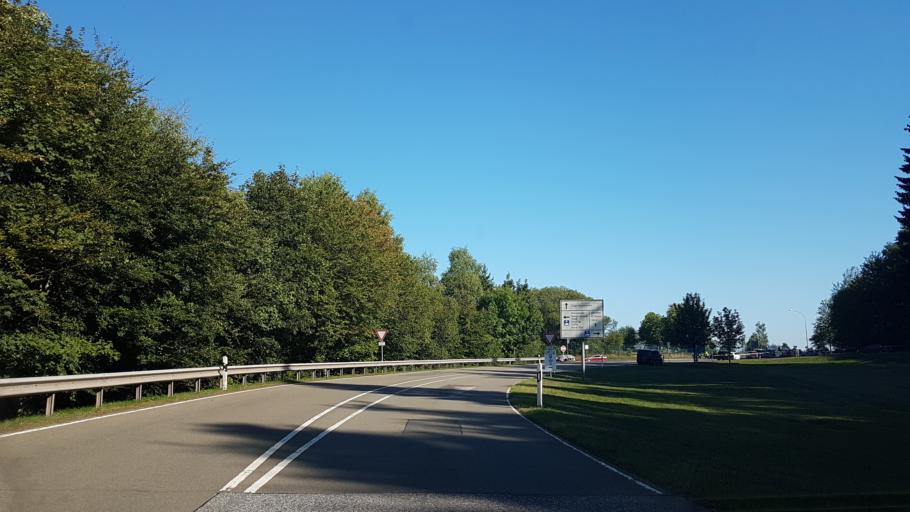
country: DE
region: Rheinland-Pfalz
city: Baumholder
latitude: 49.6347
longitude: 7.3119
